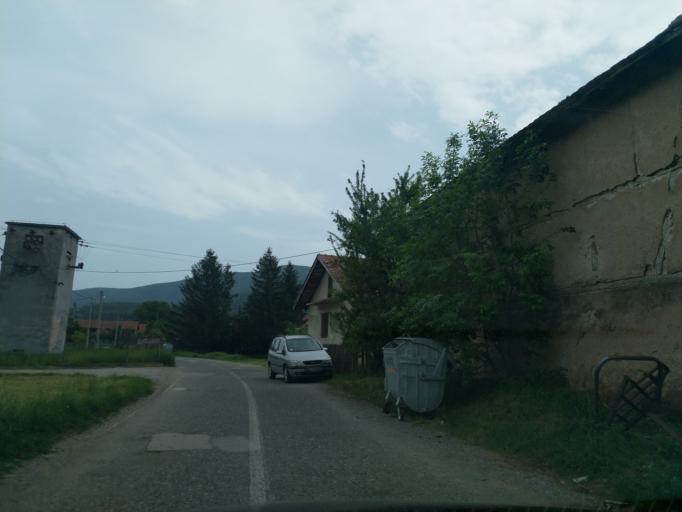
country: RS
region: Central Serbia
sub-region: Pomoravski Okrug
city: Paracin
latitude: 43.8596
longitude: 21.5911
